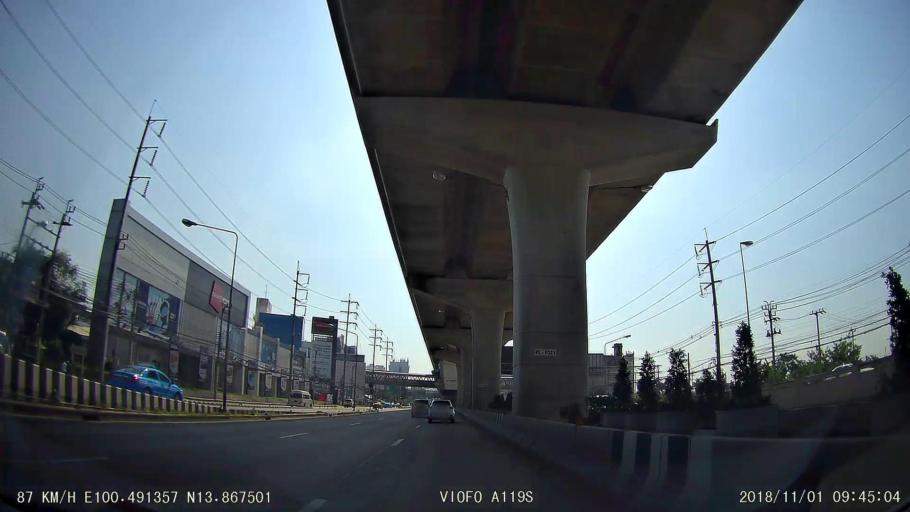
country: TH
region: Nonthaburi
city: Mueang Nonthaburi
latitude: 13.8674
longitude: 100.4915
